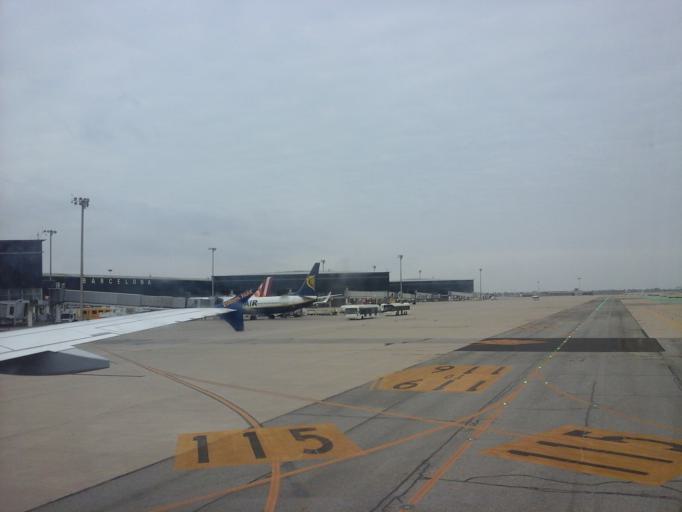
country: ES
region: Catalonia
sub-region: Provincia de Barcelona
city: El Prat de Llobregat
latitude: 41.3003
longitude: 2.0767
